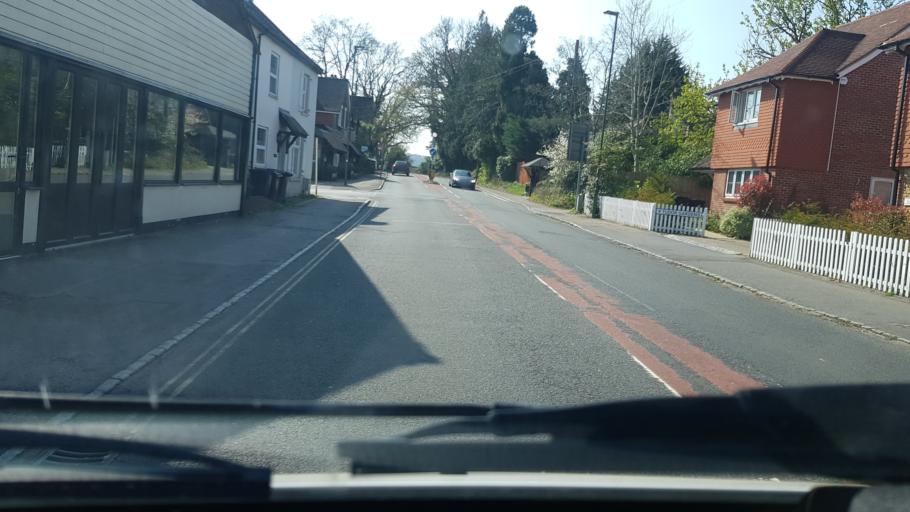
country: GB
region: England
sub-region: West Sussex
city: Fernhurst
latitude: 51.0482
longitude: -0.7229
